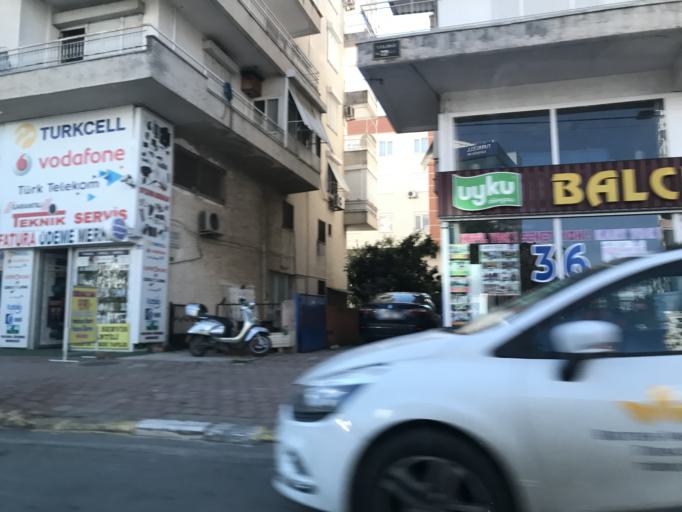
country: TR
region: Antalya
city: Antalya
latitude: 36.8990
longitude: 30.7074
